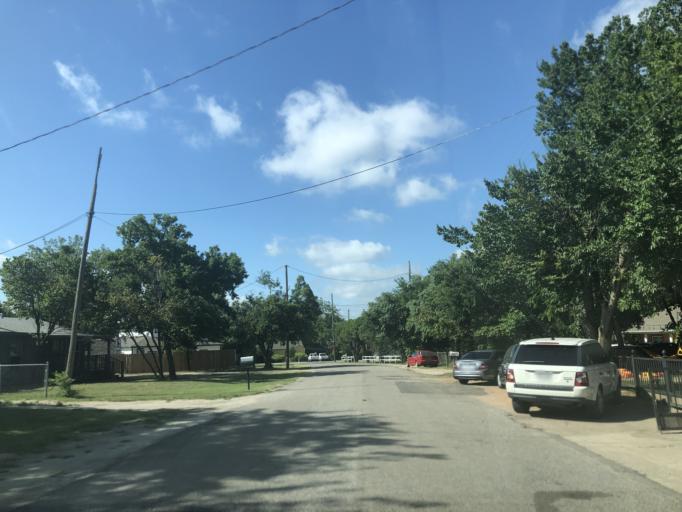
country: US
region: Texas
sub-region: Dallas County
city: Duncanville
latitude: 32.6373
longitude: -96.9055
